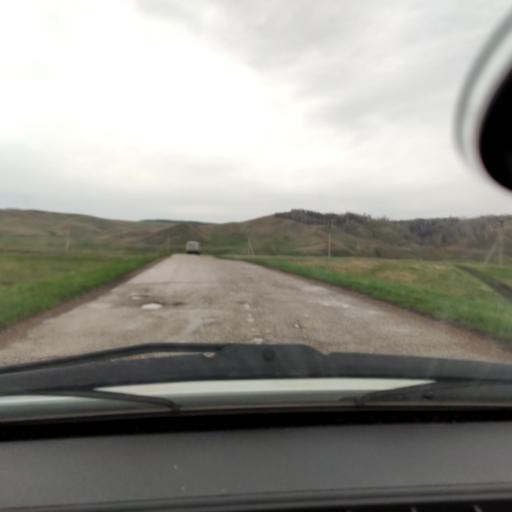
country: RU
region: Bashkortostan
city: Tolbazy
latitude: 54.1718
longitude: 55.9473
